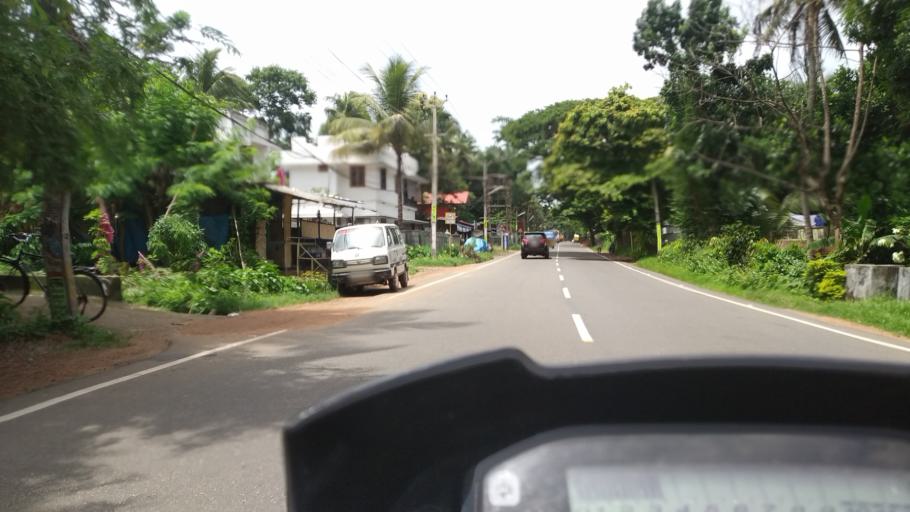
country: IN
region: Kerala
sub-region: Ernakulam
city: Aluva
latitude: 10.1265
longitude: 76.3279
